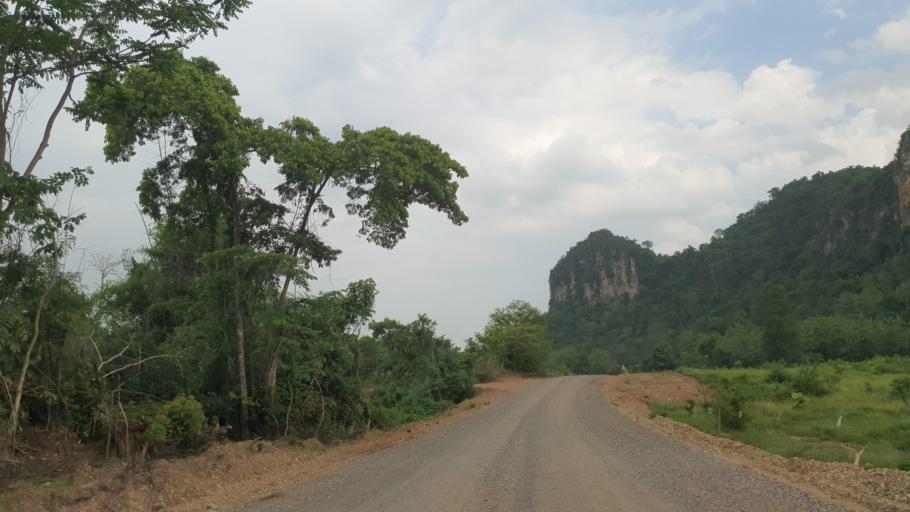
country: TH
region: Sukhothai
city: Thung Saliam
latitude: 17.2619
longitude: 99.5382
